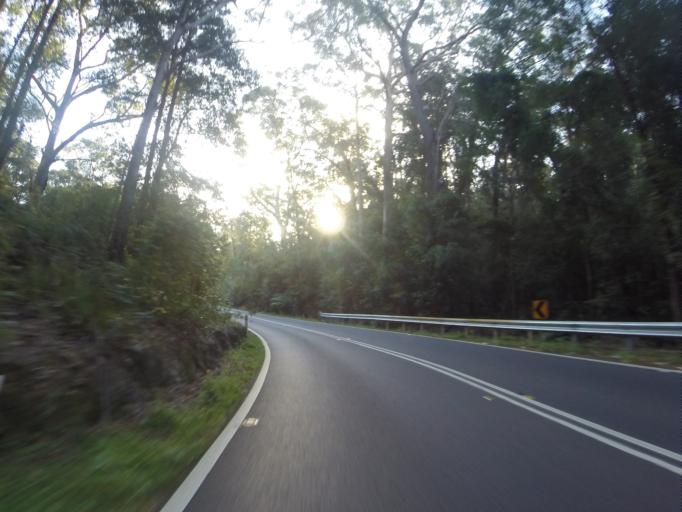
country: AU
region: New South Wales
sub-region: Shoalhaven Shire
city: Kangaroo Valley
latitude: -34.6864
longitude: 150.4938
